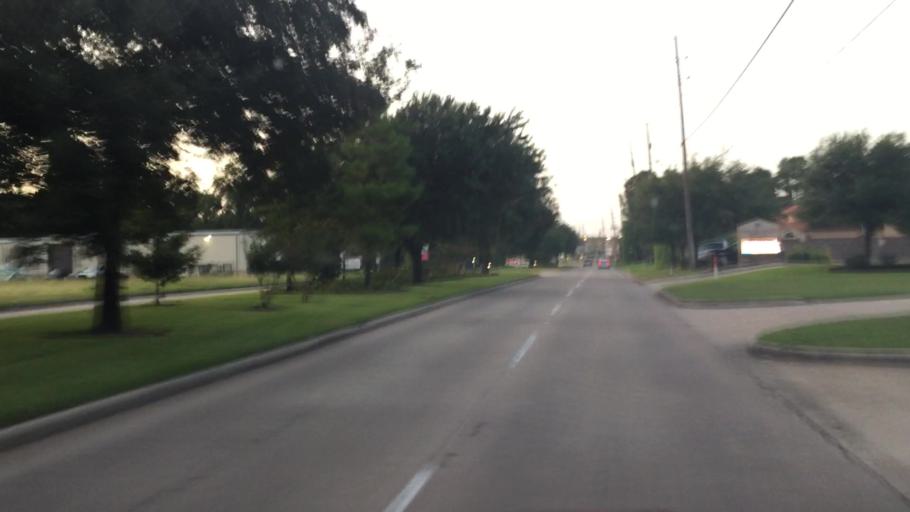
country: US
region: Texas
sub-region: Harris County
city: Tomball
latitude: 30.0257
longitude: -95.5293
